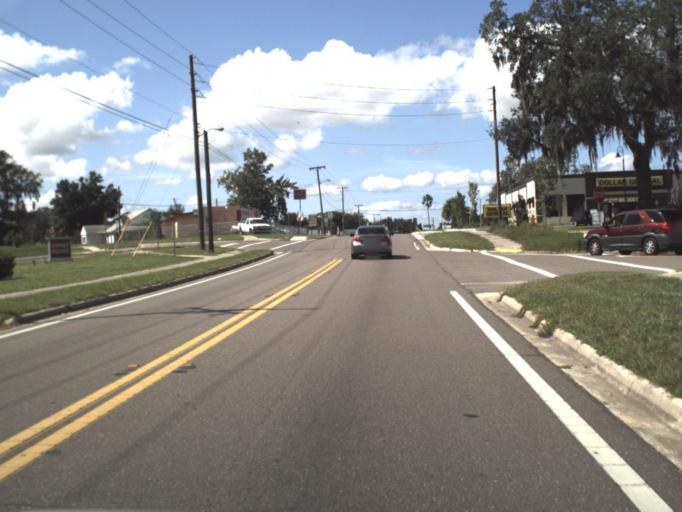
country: US
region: Florida
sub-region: Polk County
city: Davenport
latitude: 28.1622
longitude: -81.6013
